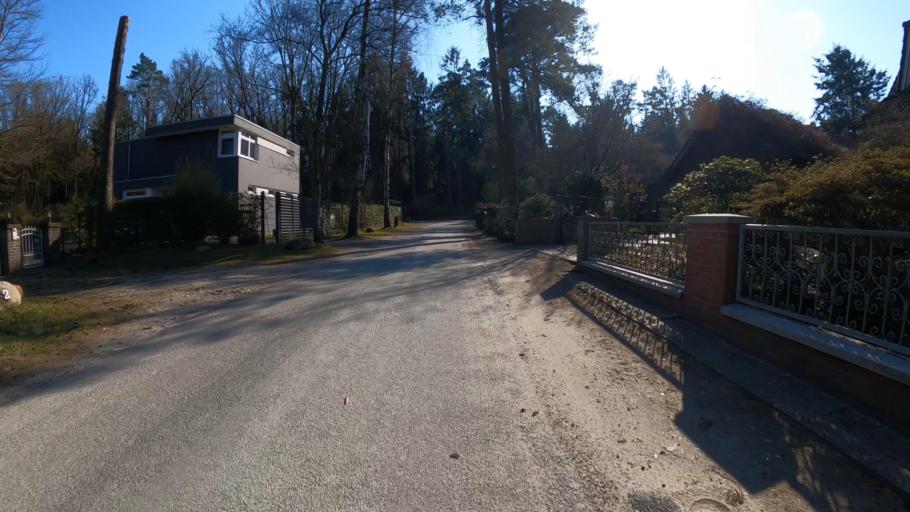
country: DE
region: Lower Saxony
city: Buchholz in der Nordheide
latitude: 53.3091
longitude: 9.8468
